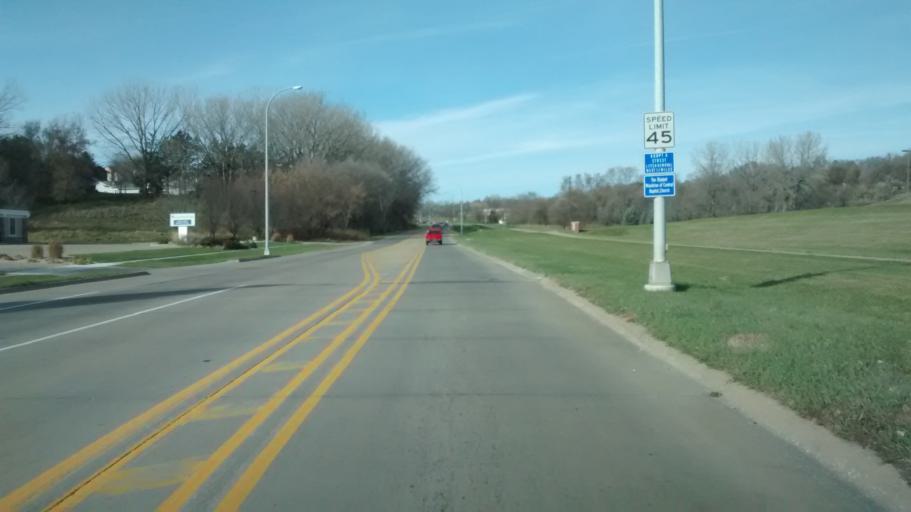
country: US
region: Iowa
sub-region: Woodbury County
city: Sioux City
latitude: 42.5371
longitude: -96.3748
